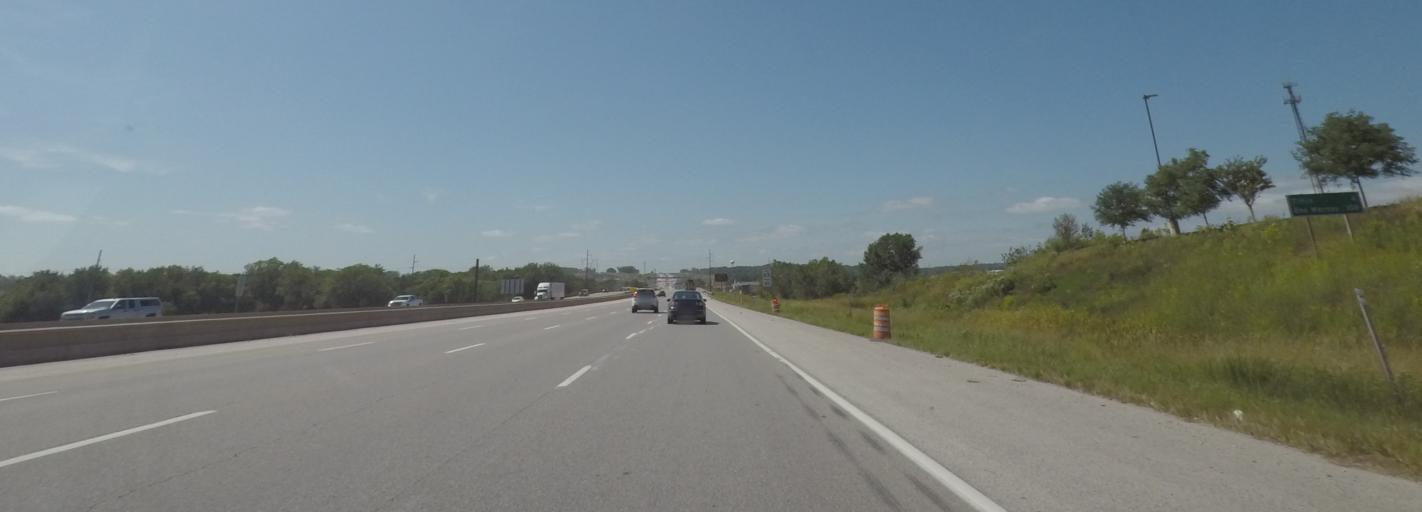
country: US
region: Iowa
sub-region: Johnson County
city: Coralville
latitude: 41.6943
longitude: -91.6163
